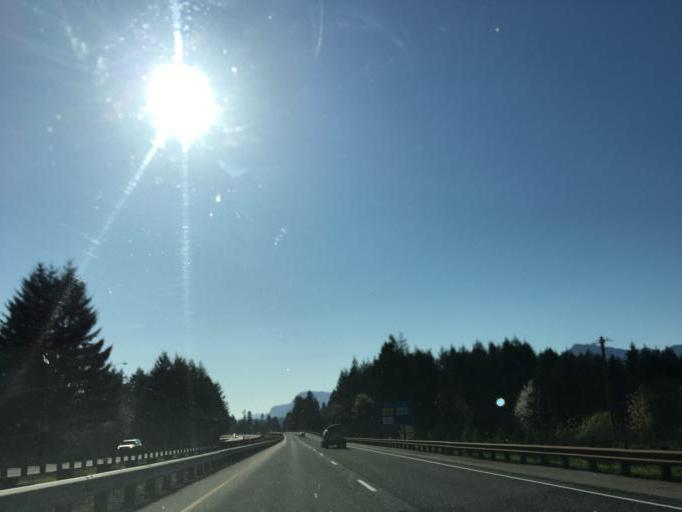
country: US
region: Oregon
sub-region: Hood River County
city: Cascade Locks
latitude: 45.6750
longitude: -121.8679
